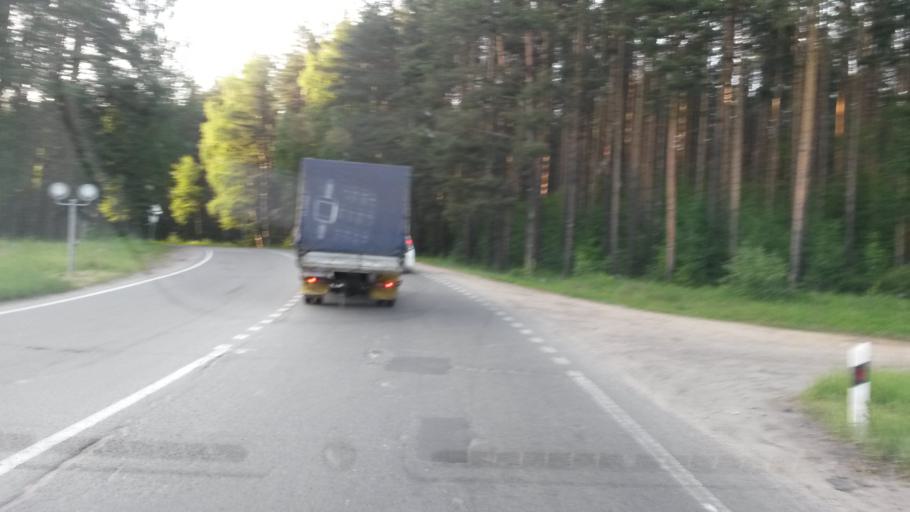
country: RU
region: Jaroslavl
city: Yaroslavl
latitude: 57.7012
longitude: 39.8623
